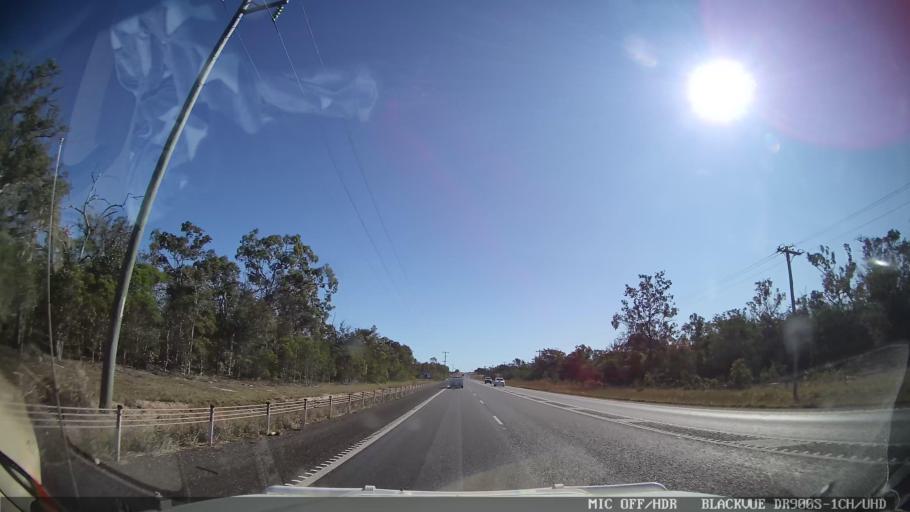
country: AU
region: Queensland
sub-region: Bundaberg
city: Childers
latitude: -25.2491
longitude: 152.3387
